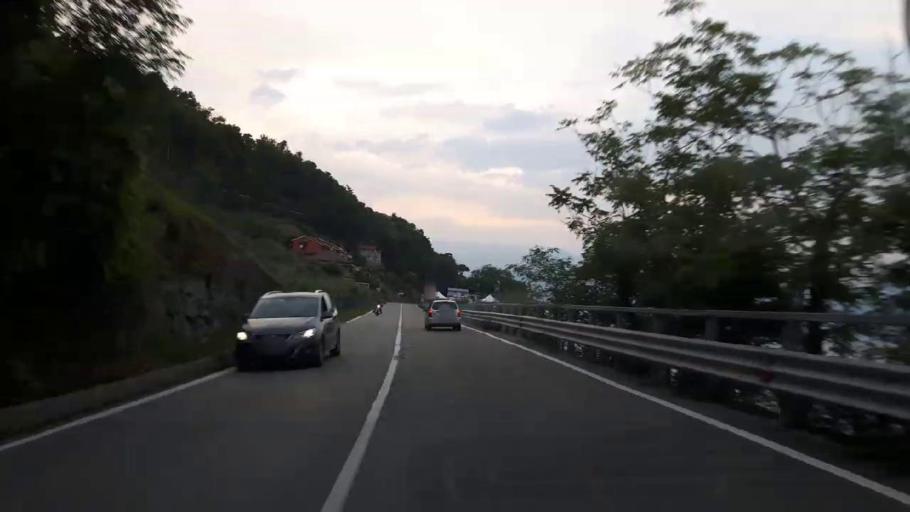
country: IT
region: Piedmont
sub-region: Provincia Verbano-Cusio-Ossola
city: Belgirate
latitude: 45.8650
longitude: 8.5672
